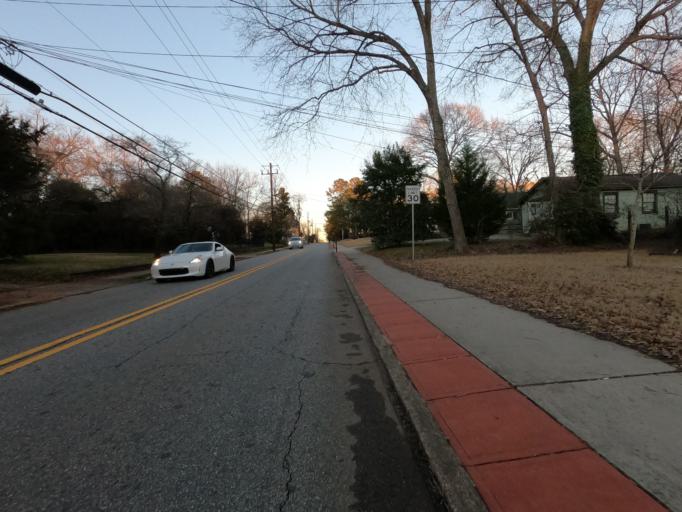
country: US
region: Georgia
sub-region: Clarke County
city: Athens
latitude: 33.9328
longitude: -83.3917
